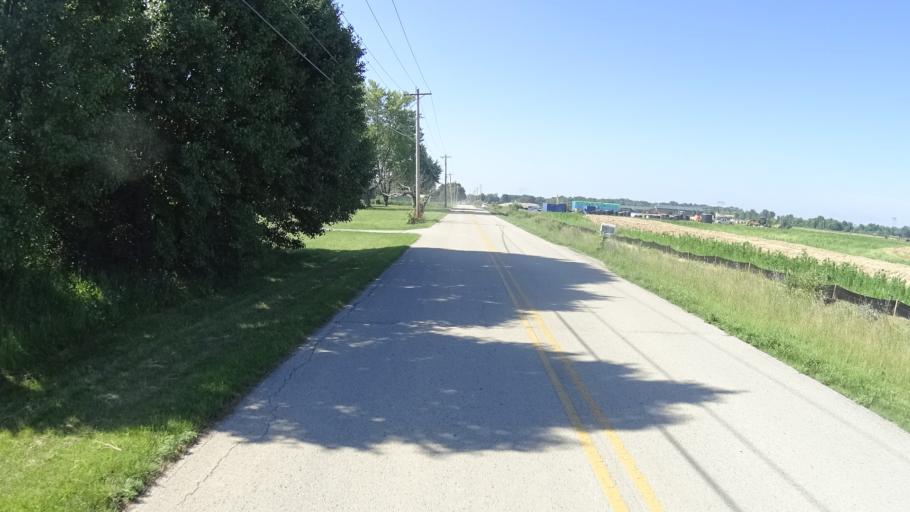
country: US
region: Indiana
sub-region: Madison County
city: Ingalls
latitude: 39.9852
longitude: -85.7962
